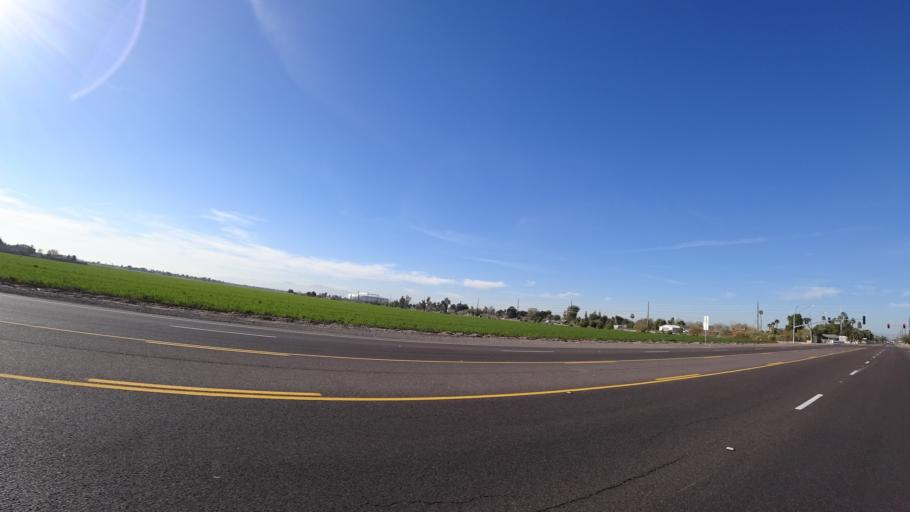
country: US
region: Arizona
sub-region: Maricopa County
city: Glendale
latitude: 33.5211
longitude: -112.2376
